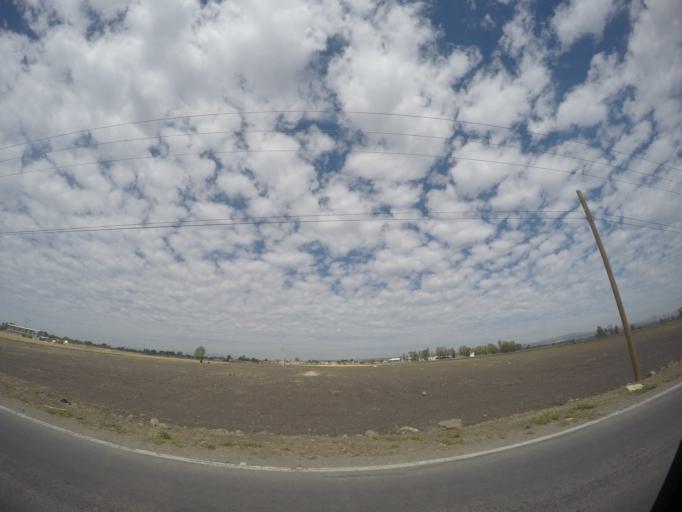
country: MX
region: Guanajuato
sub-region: Leon
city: El CERESO
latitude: 21.0298
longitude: -101.6955
